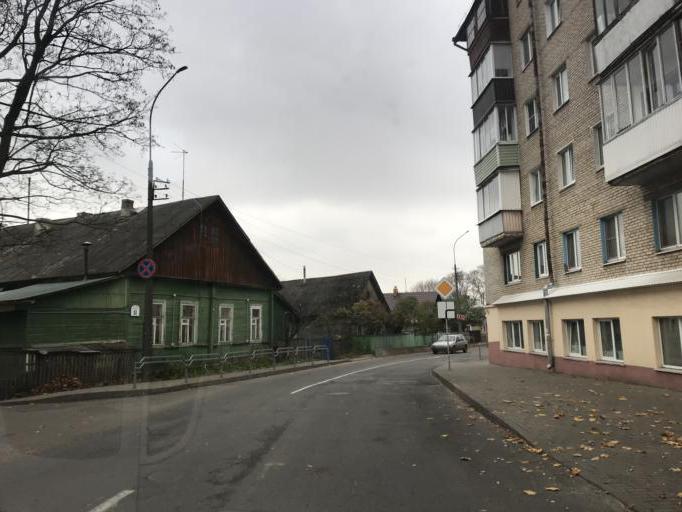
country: BY
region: Mogilev
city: Mahilyow
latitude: 53.9031
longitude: 30.3454
